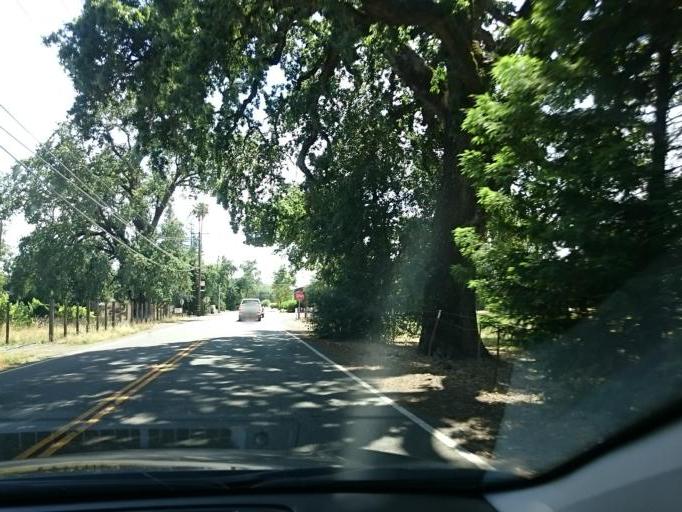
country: US
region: California
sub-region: Sonoma County
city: Healdsburg
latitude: 38.6670
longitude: -122.8191
